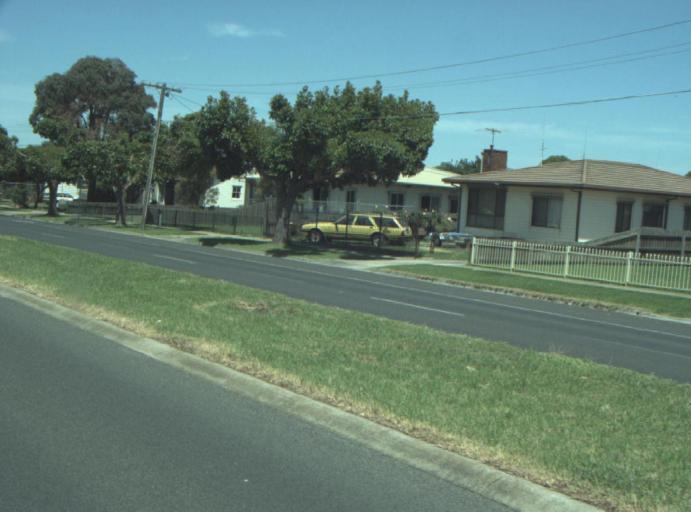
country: AU
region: Victoria
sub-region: Greater Geelong
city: Bell Park
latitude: -38.0974
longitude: 144.3652
